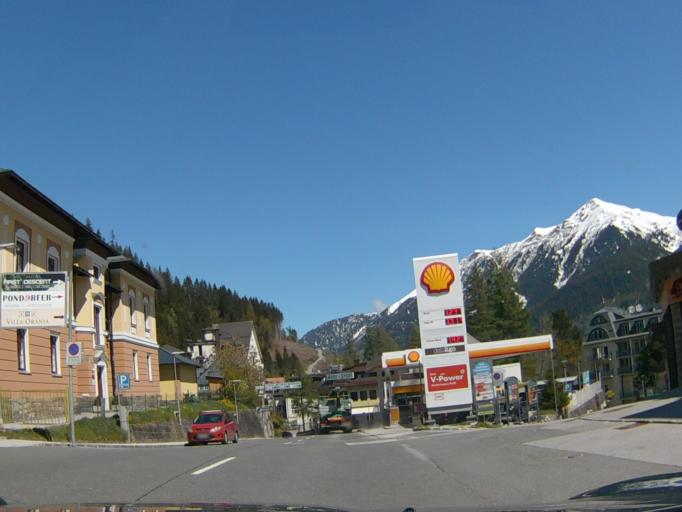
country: AT
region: Salzburg
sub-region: Politischer Bezirk Sankt Johann im Pongau
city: Bad Gastein
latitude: 47.1124
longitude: 13.1325
